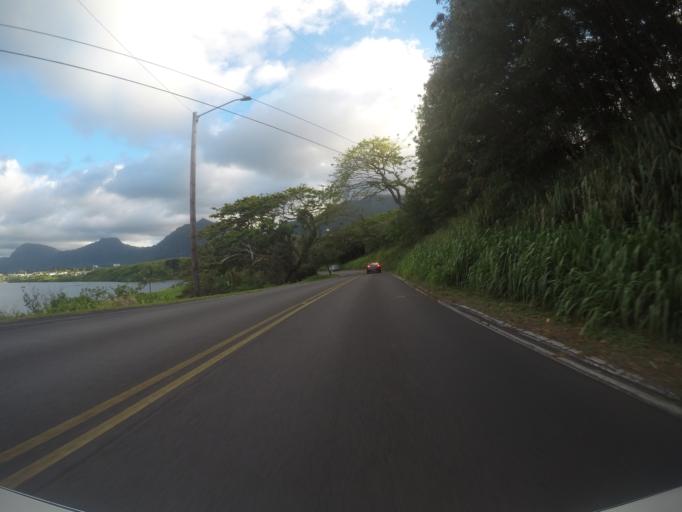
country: US
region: Hawaii
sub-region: Honolulu County
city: He'eia
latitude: 21.4406
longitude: -157.8102
